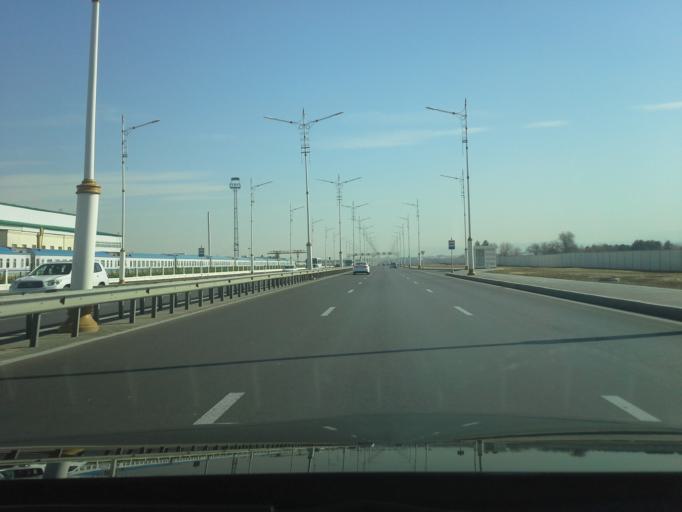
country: TM
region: Ahal
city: Ashgabat
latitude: 37.9354
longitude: 58.4103
